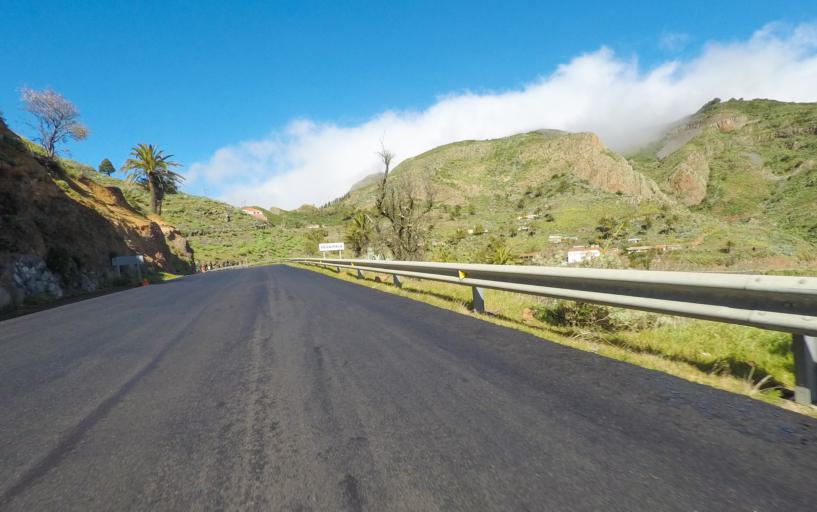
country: ES
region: Canary Islands
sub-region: Provincia de Santa Cruz de Tenerife
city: Alajero
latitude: 28.0919
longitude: -17.2019
